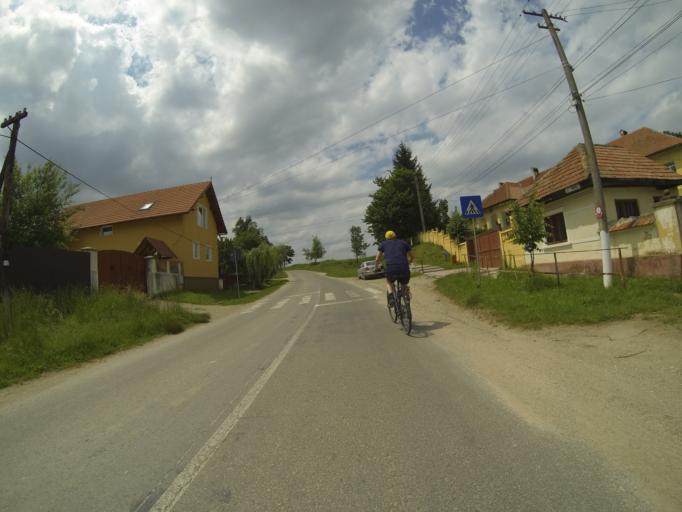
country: RO
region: Brasov
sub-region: Comuna Sinca Veche
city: Sinca Veche
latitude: 45.7459
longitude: 25.1188
